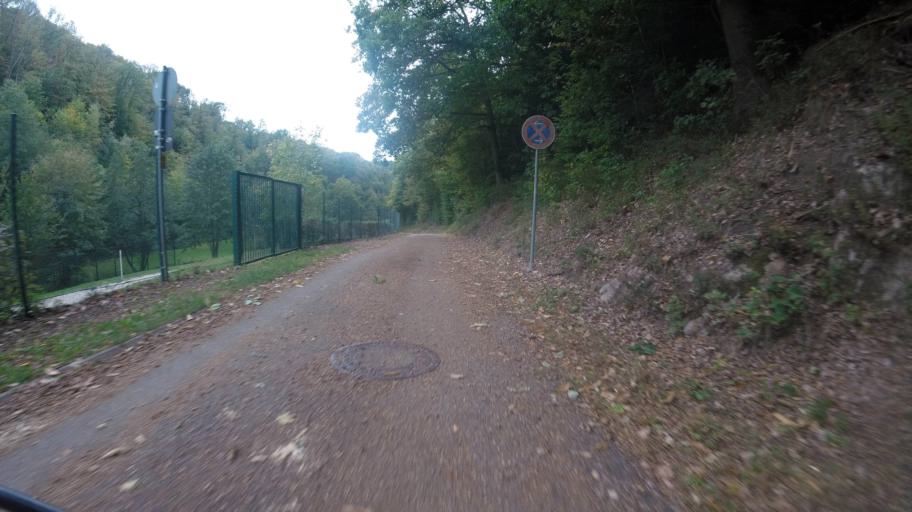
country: DE
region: Baden-Wuerttemberg
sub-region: Karlsruhe Region
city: Gernsbach
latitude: 48.7631
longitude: 8.3519
